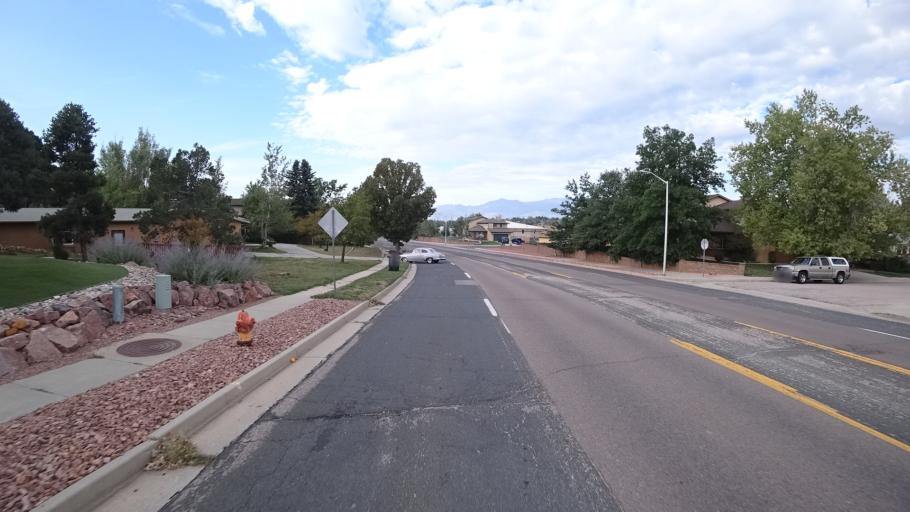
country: US
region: Colorado
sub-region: El Paso County
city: Cimarron Hills
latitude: 38.8698
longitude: -104.7518
